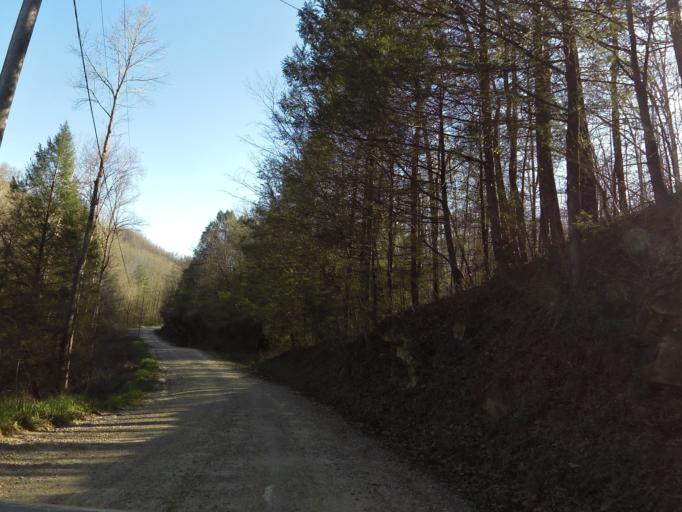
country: US
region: Tennessee
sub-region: Scott County
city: Huntsville
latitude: 36.2430
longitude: -84.4124
